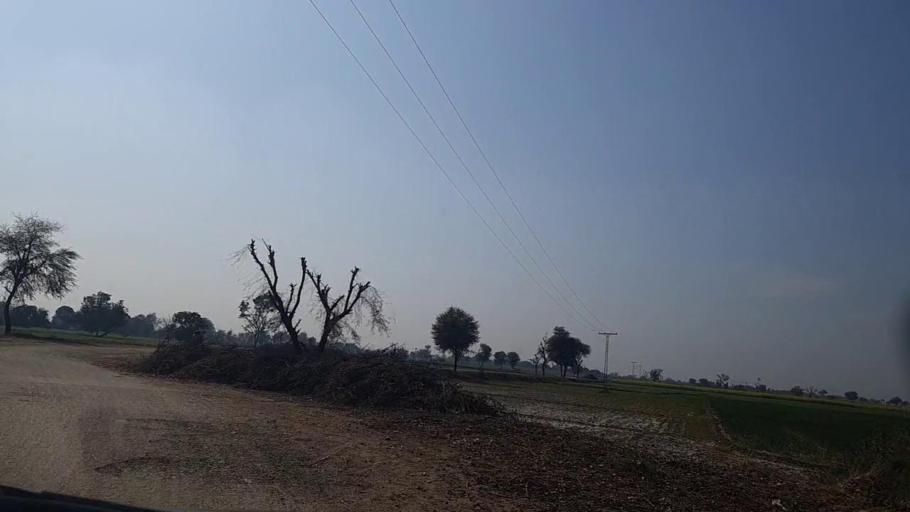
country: PK
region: Sindh
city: Sakrand
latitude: 26.0316
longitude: 68.4092
